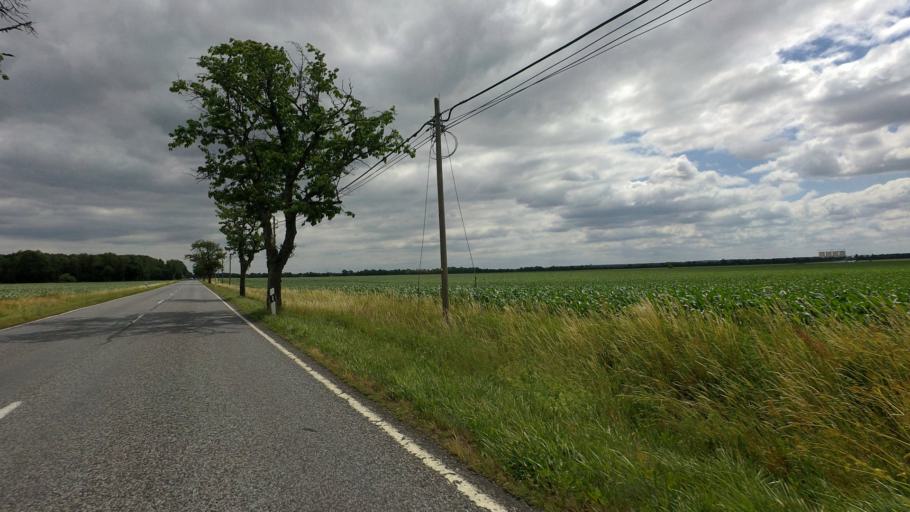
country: DE
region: Brandenburg
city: Luckau
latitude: 51.8307
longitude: 13.7750
